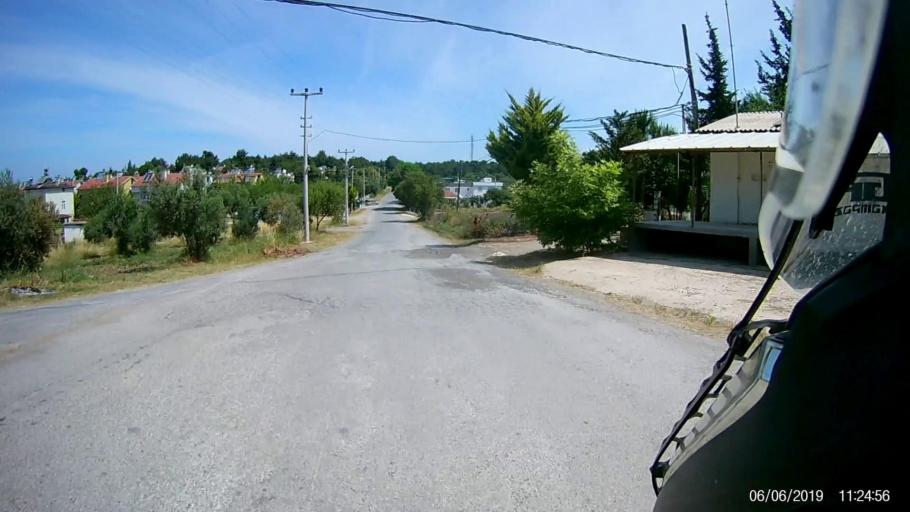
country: TR
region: Canakkale
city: Gulpinar
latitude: 39.6263
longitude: 26.1820
